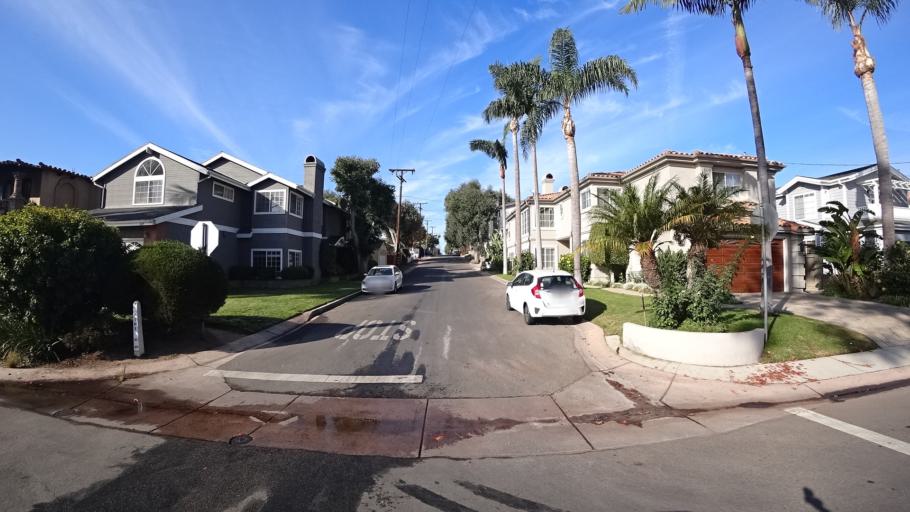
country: US
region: California
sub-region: Los Angeles County
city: Manhattan Beach
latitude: 33.8903
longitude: -118.3987
